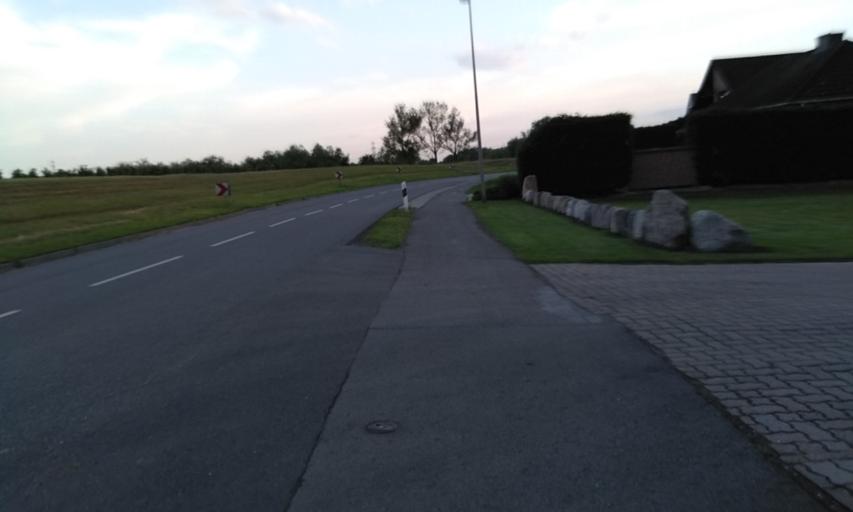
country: DE
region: Lower Saxony
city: Buxtehude
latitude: 53.4998
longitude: 9.7237
